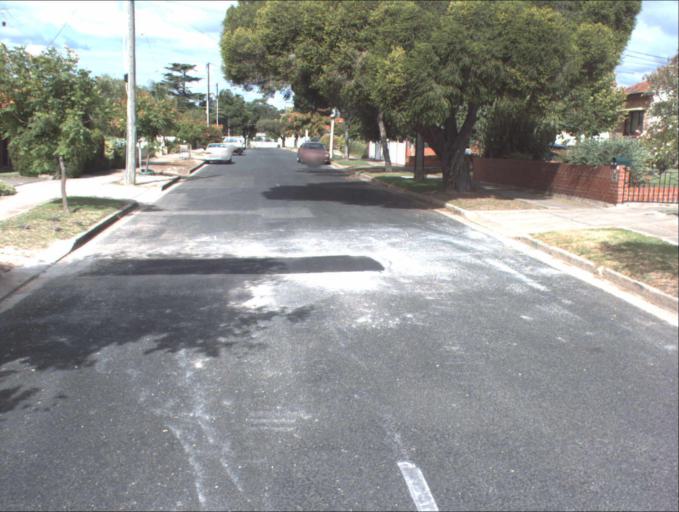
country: AU
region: South Australia
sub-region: Port Adelaide Enfield
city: Blair Athol
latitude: -34.8682
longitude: 138.5957
